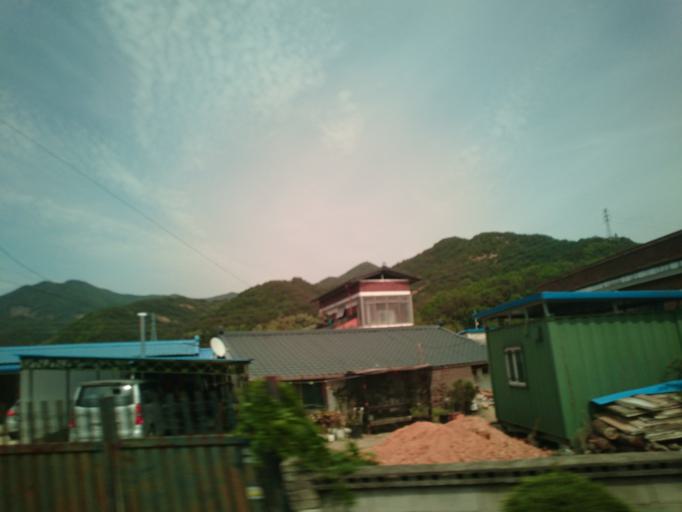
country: KR
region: Jeollabuk-do
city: Wanju
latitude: 35.8965
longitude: 127.1916
